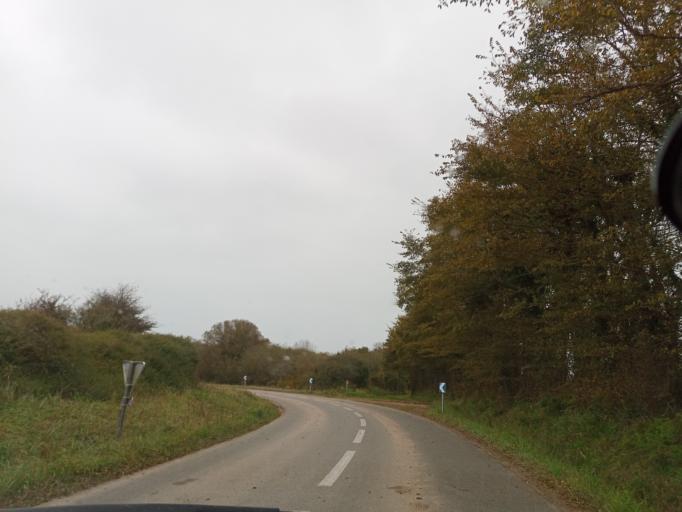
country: FR
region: Brittany
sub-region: Departement du Finistere
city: Esquibien
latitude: 48.0189
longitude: -4.5635
